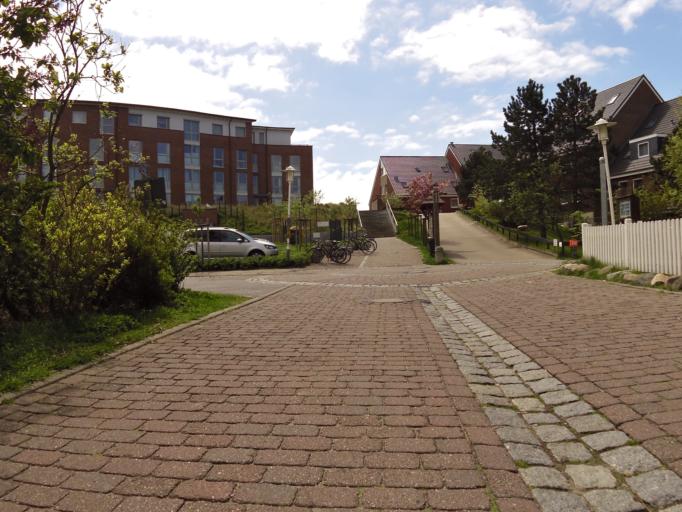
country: DE
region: Schleswig-Holstein
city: Wittdun
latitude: 54.6259
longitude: 8.3921
